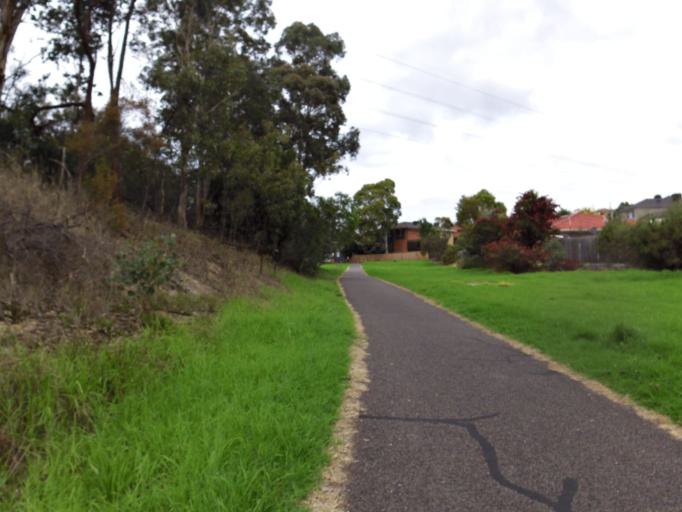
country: AU
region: Victoria
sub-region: Nillumbik
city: Eltham
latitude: -37.7595
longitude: 145.1620
